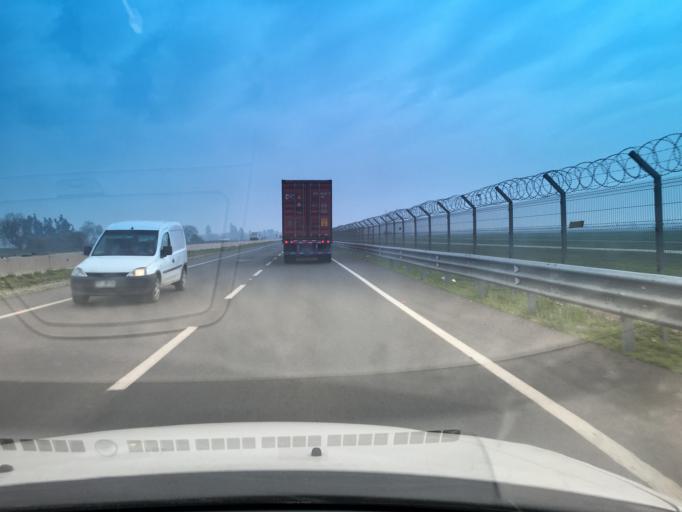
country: CL
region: Santiago Metropolitan
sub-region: Provincia de Santiago
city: Lo Prado
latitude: -33.3778
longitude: -70.8051
